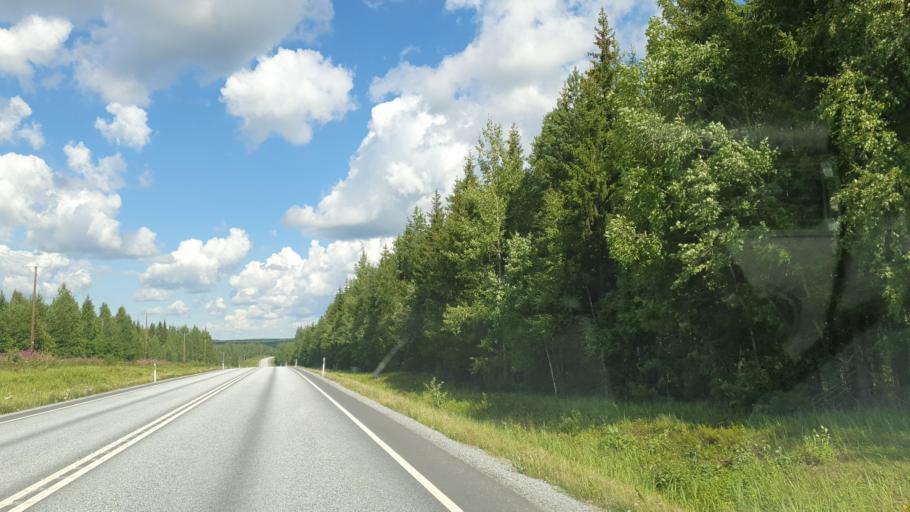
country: FI
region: Northern Savo
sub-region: Ylae-Savo
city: Sonkajaervi
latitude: 63.9591
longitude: 27.3755
